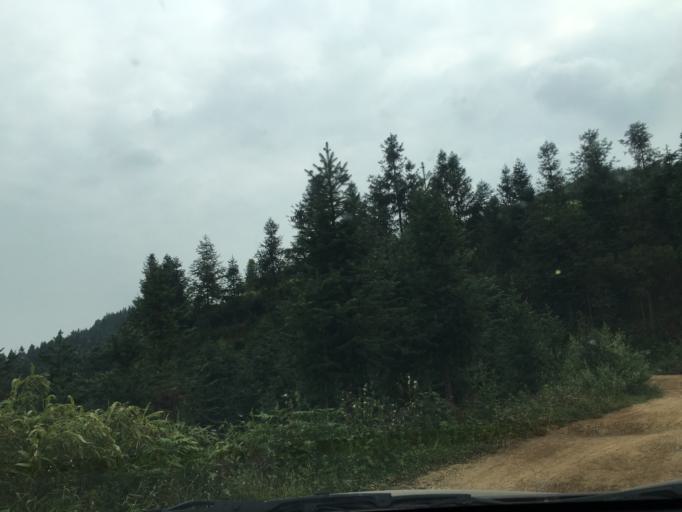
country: CN
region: Guangxi Zhuangzu Zizhiqu
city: Xinzhou
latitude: 25.5438
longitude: 105.5330
